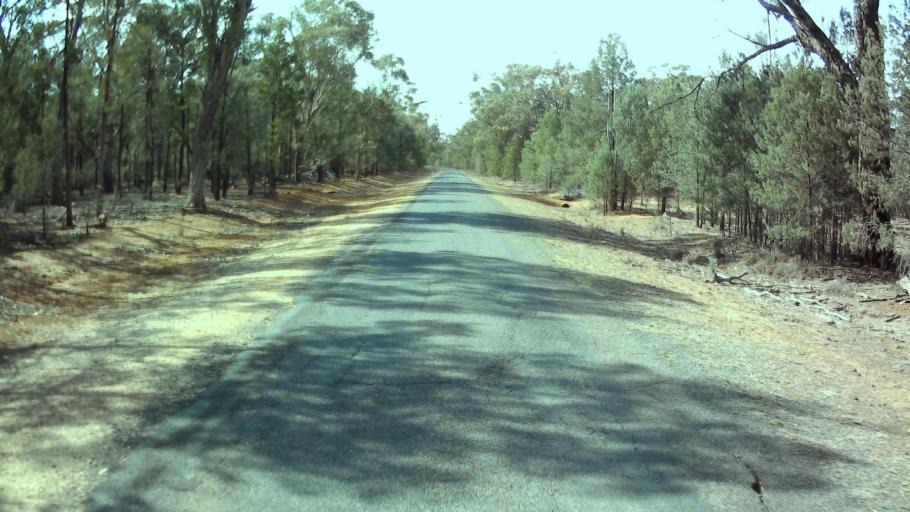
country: AU
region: New South Wales
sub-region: Weddin
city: Grenfell
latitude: -33.7207
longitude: 148.0281
